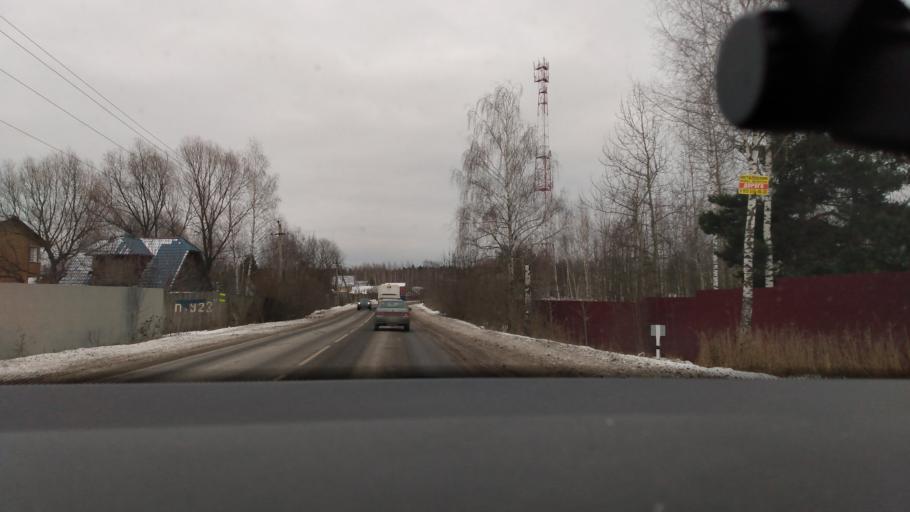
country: RU
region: Moskovskaya
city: Rodniki
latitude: 55.6925
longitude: 38.0738
